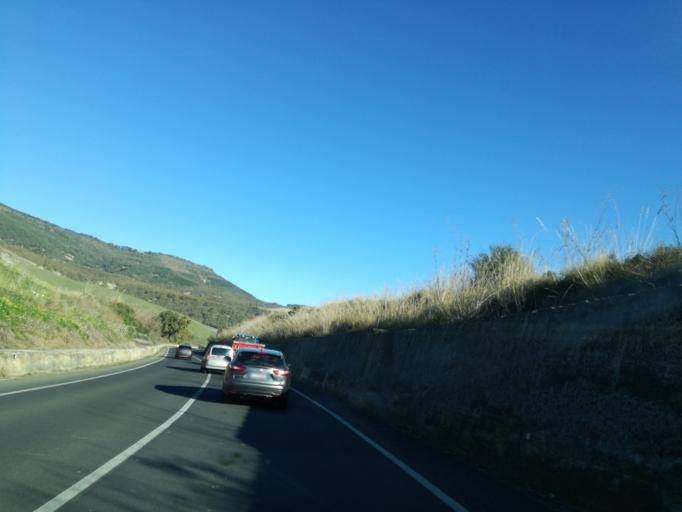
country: IT
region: Sicily
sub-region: Catania
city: San Michele di Ganzaria
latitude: 37.2360
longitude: 14.4500
